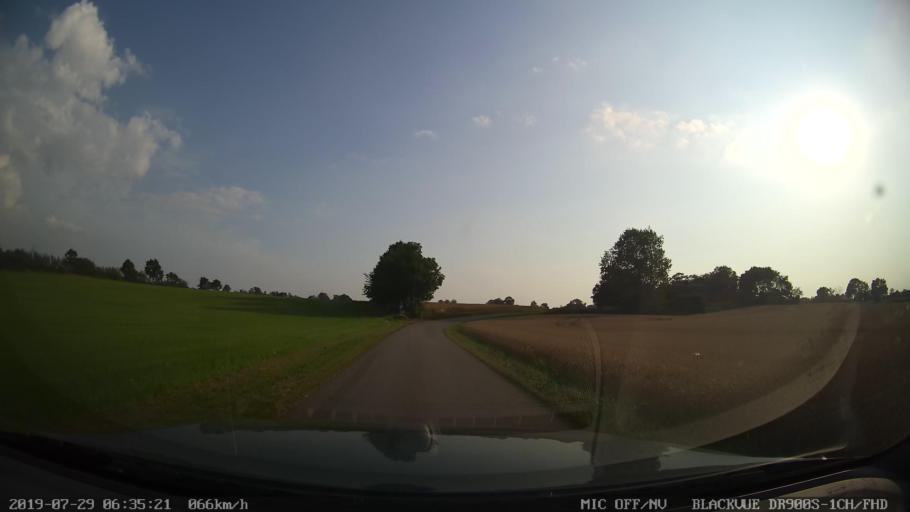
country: SE
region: Skane
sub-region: Helsingborg
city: Odakra
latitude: 56.1135
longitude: 12.7186
